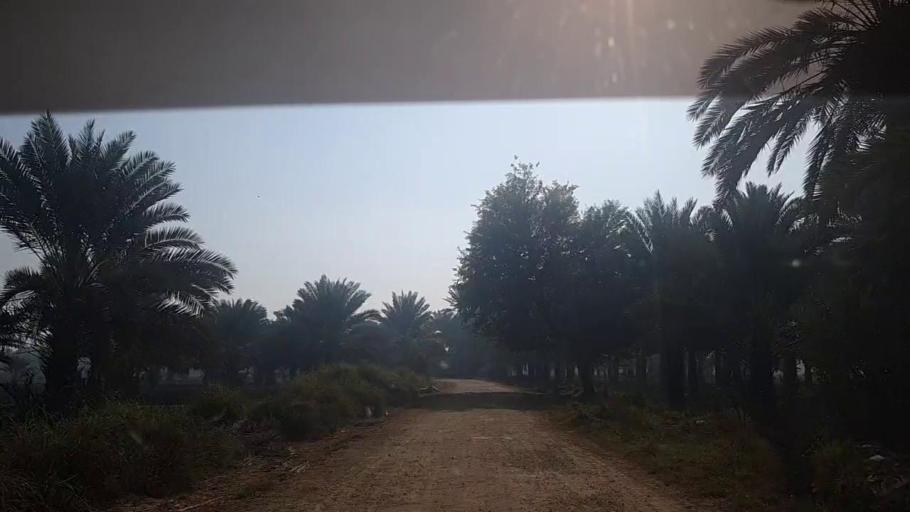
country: PK
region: Sindh
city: Khairpur
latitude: 27.4776
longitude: 68.7218
